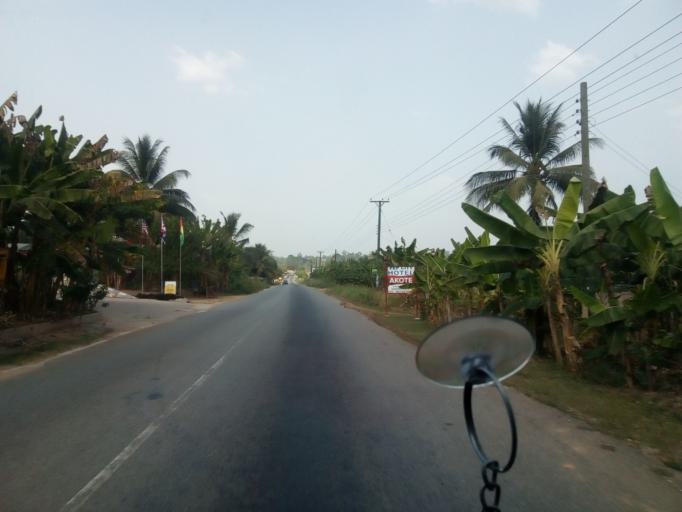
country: GH
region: Eastern
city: Suhum
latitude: 6.0592
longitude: -0.4021
